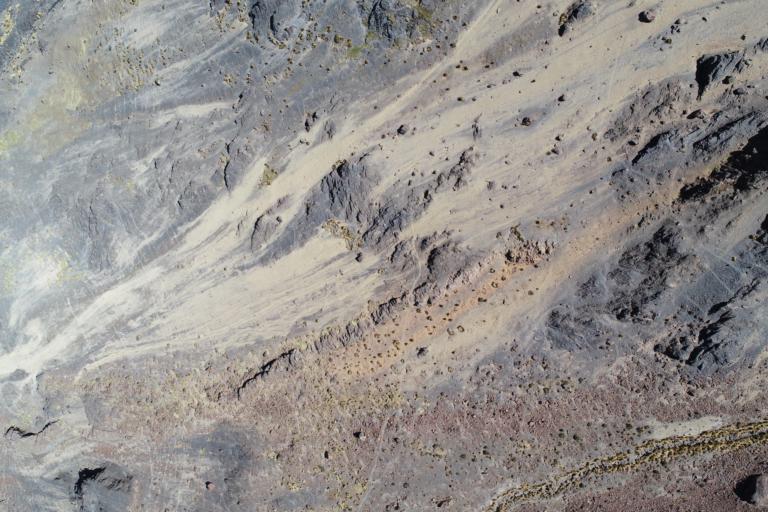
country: BO
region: La Paz
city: La Paz
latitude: -16.6195
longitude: -67.8233
